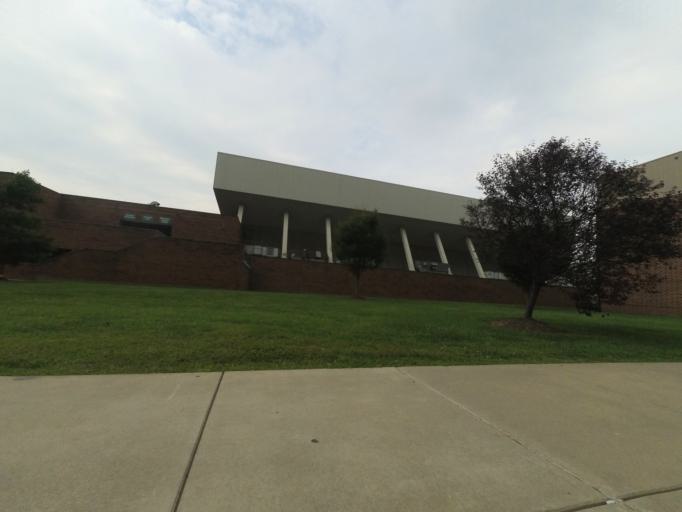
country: US
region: West Virginia
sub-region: Cabell County
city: Huntington
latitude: 38.4237
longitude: -82.4253
